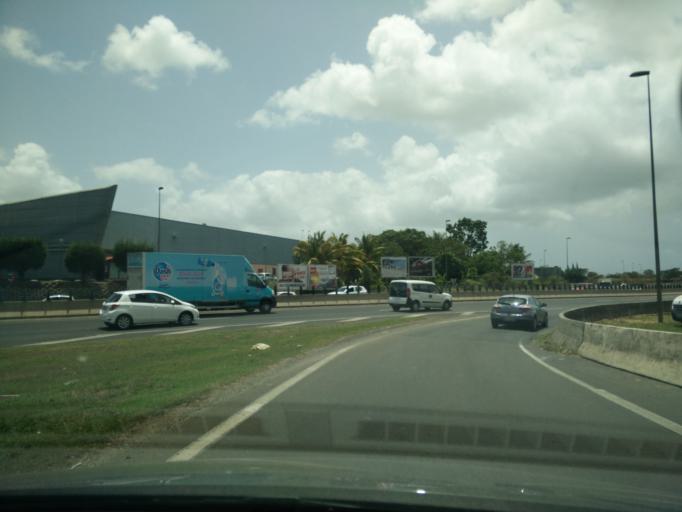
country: GP
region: Guadeloupe
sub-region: Guadeloupe
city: Les Abymes
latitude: 16.2661
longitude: -61.5112
